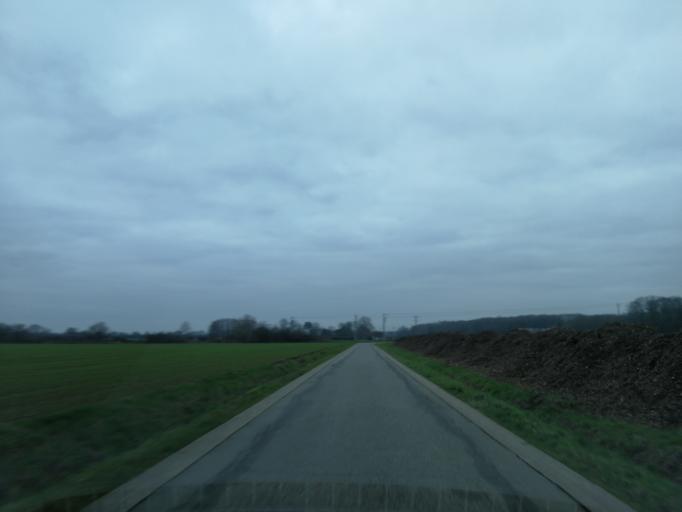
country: FR
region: Ile-de-France
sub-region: Departement de l'Essonne
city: Les Molieres
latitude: 48.6653
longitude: 2.0850
